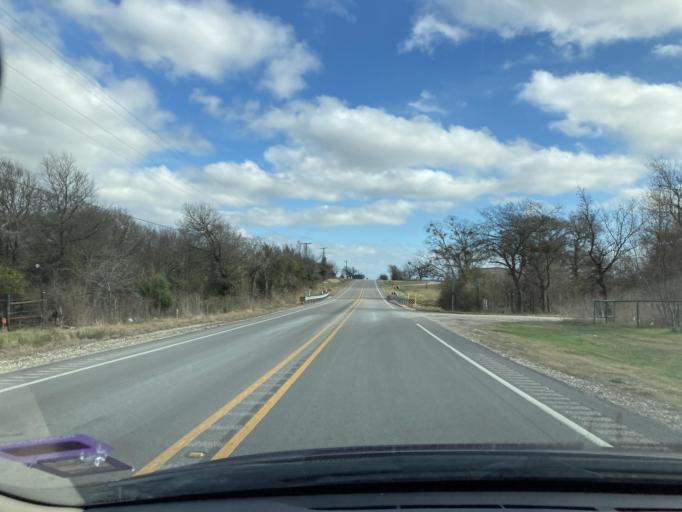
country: US
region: Texas
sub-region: Navarro County
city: Corsicana
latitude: 32.0543
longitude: -96.3697
